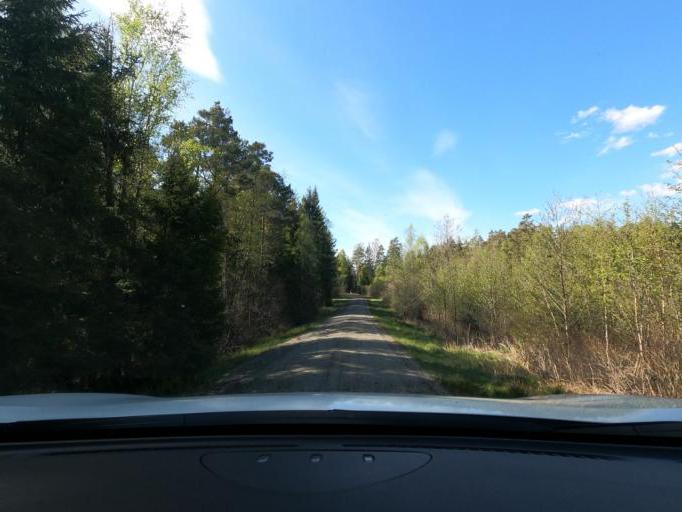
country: SE
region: Vaestra Goetaland
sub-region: Harryda Kommun
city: Ravlanda
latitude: 57.5932
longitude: 12.4822
